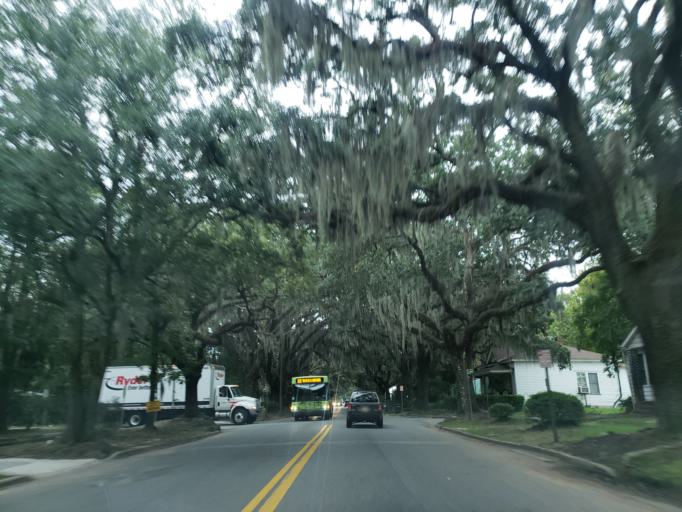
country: US
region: Georgia
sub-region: Chatham County
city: Savannah
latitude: 32.0546
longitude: -81.0902
